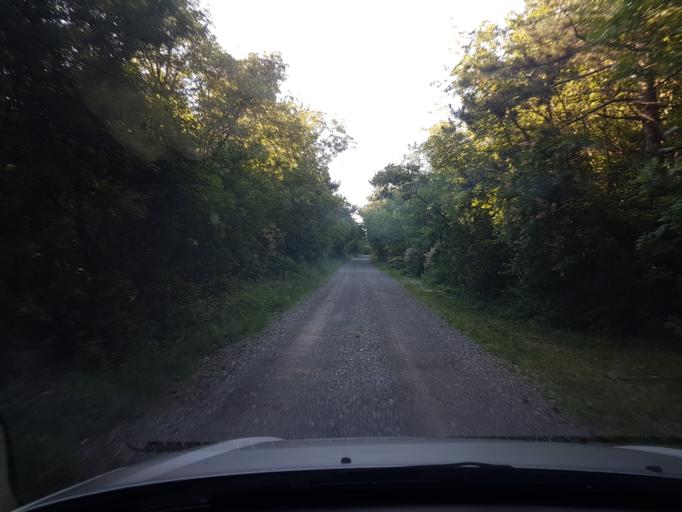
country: SI
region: Sezana
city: Sezana
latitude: 45.7203
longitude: 13.9098
